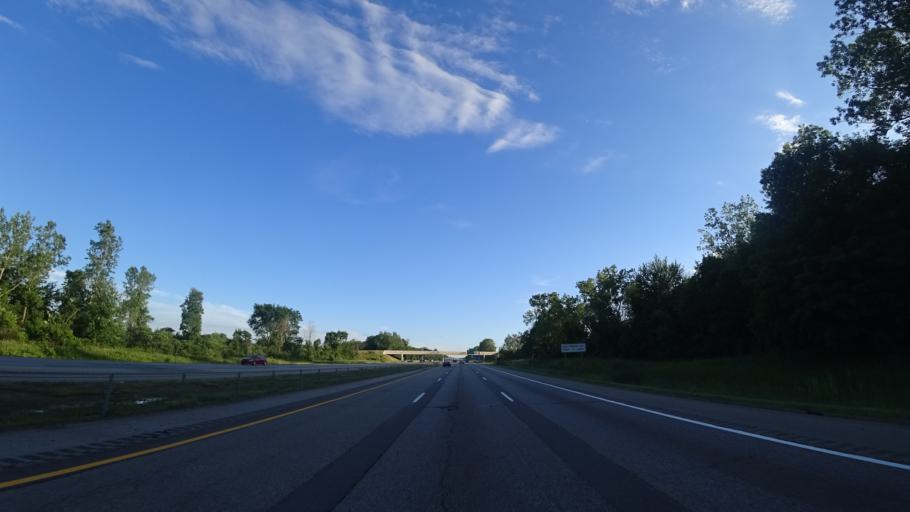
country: US
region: Michigan
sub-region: Berrien County
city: Benton Heights
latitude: 42.1110
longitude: -86.3966
